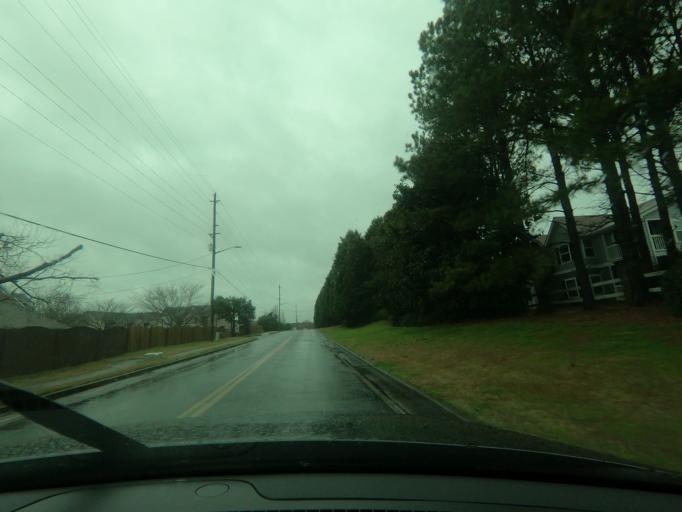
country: US
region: Georgia
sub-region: Cobb County
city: Acworth
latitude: 34.0720
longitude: -84.6495
